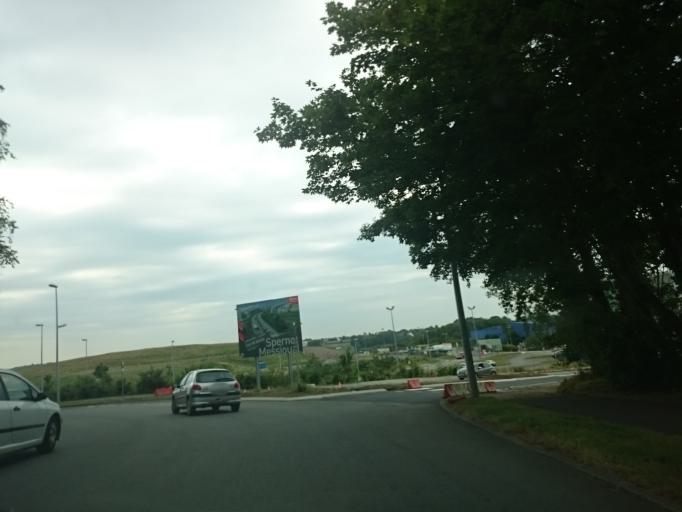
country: FR
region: Brittany
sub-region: Departement du Finistere
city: Bohars
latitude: 48.4132
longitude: -4.5078
